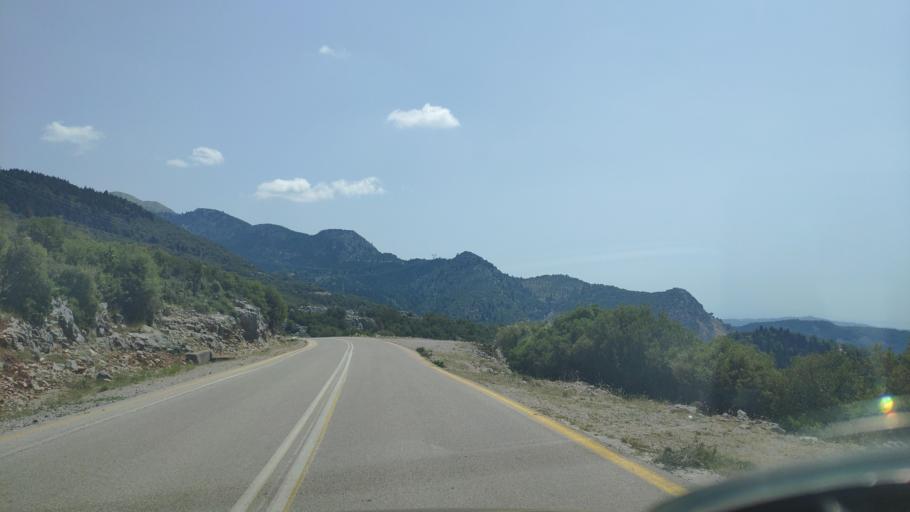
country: GR
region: Epirus
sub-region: Nomos Artas
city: Ano Kalentini
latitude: 39.2631
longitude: 21.2496
